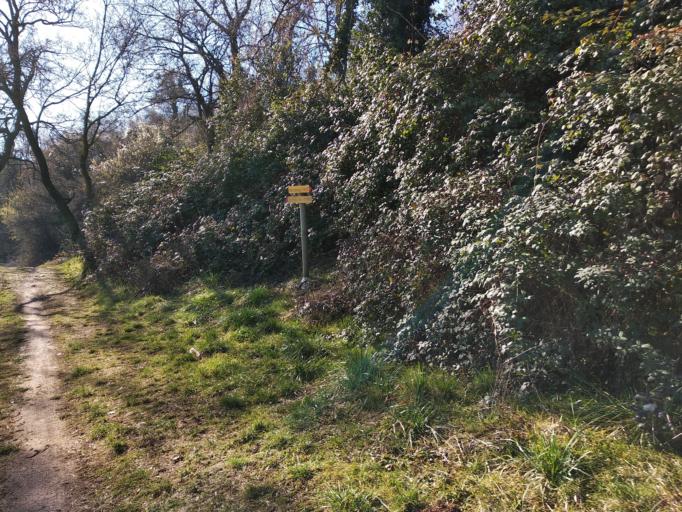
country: IT
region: Veneto
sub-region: Provincia di Vicenza
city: Gambugliano
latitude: 45.5921
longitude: 11.4552
